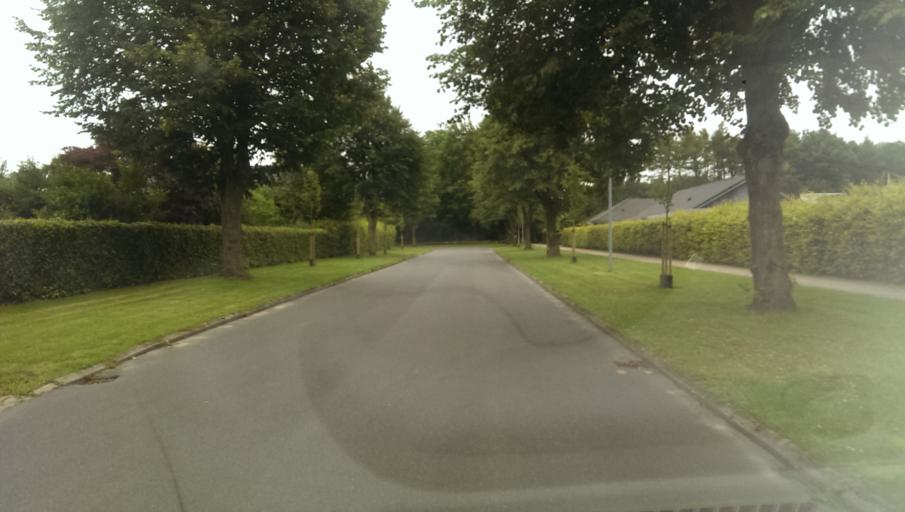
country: DK
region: South Denmark
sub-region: Esbjerg Kommune
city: Bramming
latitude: 55.4749
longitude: 8.6890
